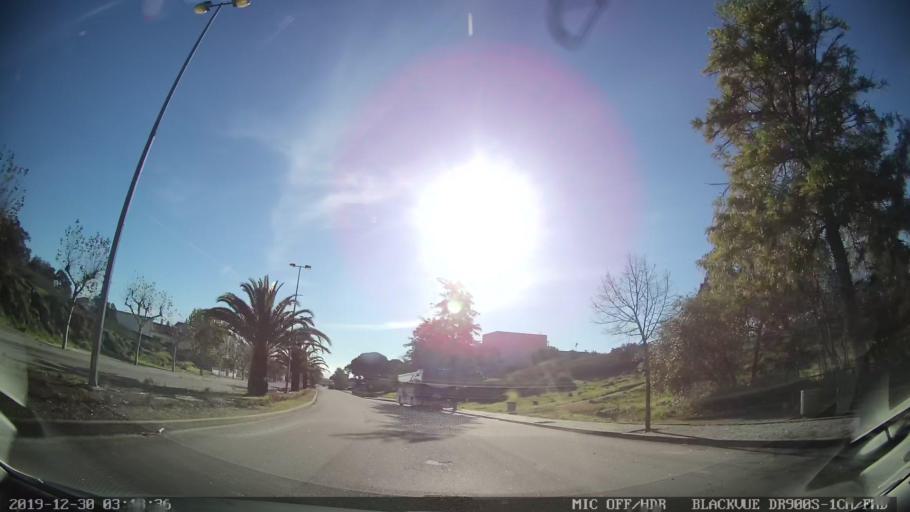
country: PT
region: Castelo Branco
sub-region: Idanha-A-Nova
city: Idanha-a-Nova
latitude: 39.9280
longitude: -7.2434
